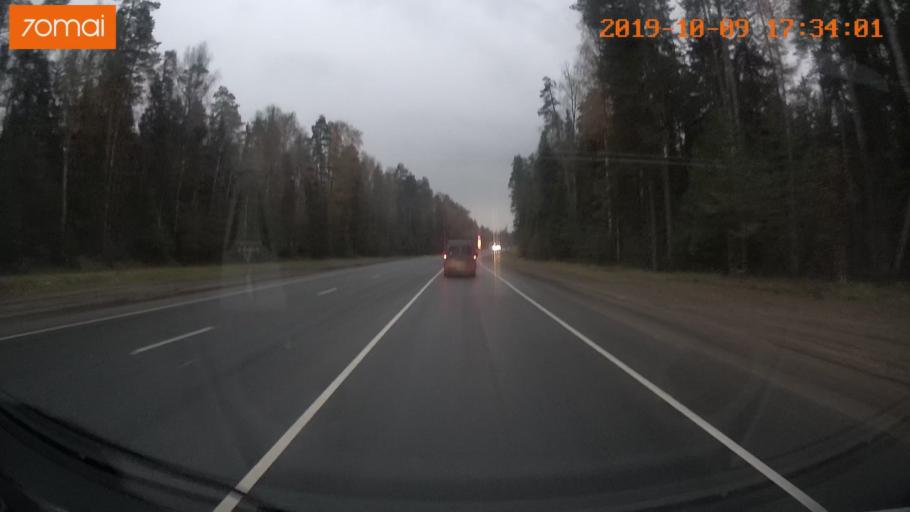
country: RU
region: Ivanovo
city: Bogorodskoye
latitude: 57.1106
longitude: 41.0158
